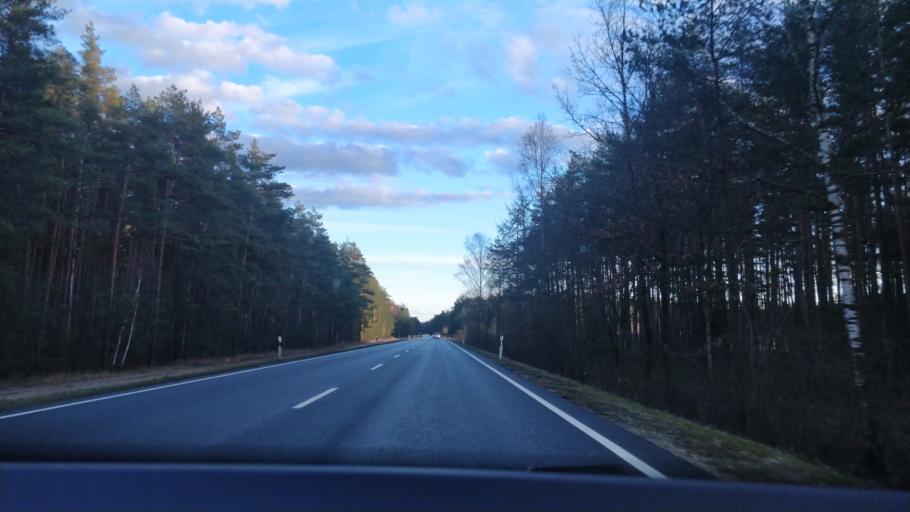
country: DE
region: Bavaria
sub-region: Upper Palatinate
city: Pressath
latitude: 49.7425
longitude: 11.9447
